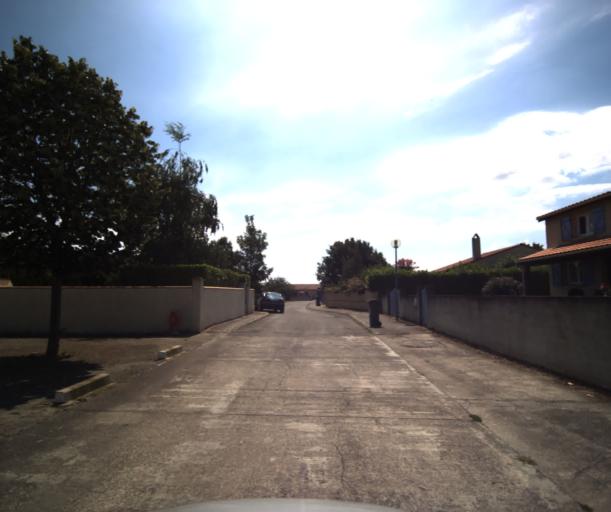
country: FR
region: Midi-Pyrenees
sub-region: Departement de la Haute-Garonne
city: Lacasse
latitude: 43.3904
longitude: 1.2544
